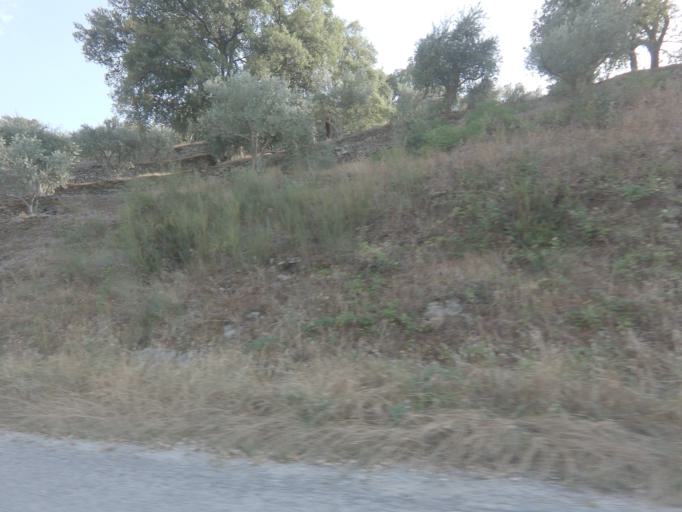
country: PT
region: Viseu
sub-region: Tabuaco
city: Tabuaco
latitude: 41.1309
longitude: -7.5369
